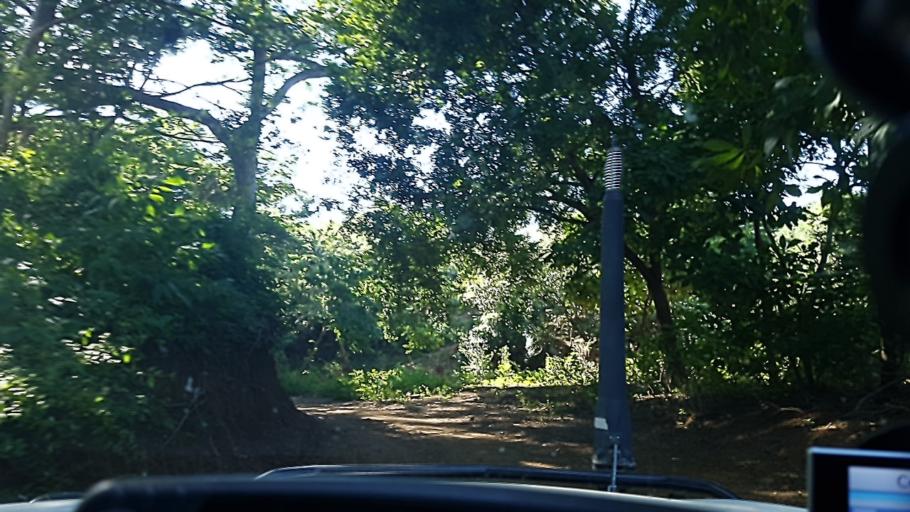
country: NI
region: Rivas
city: Tola
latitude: 11.5421
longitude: -86.1145
